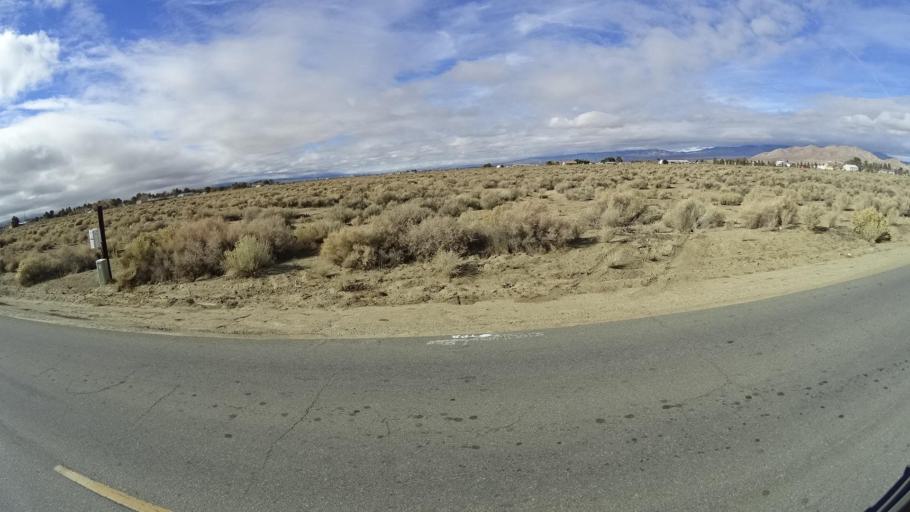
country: US
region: California
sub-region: Kern County
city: Rosamond
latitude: 34.8450
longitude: -118.2378
